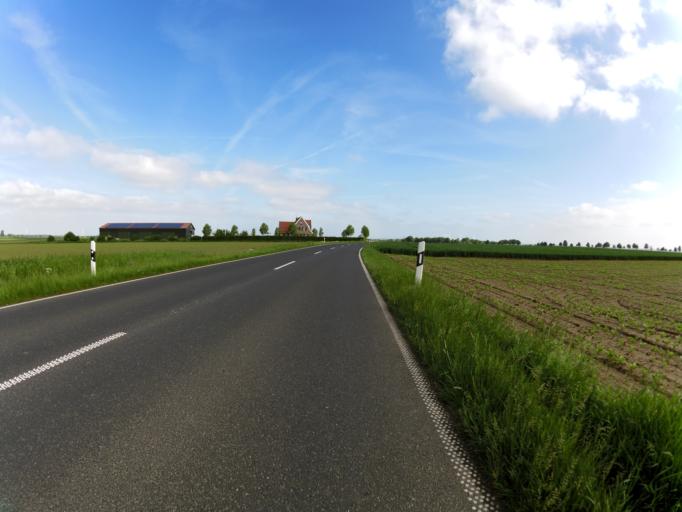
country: DE
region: North Rhine-Westphalia
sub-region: Regierungsbezirk Koln
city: Linnich
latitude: 50.9860
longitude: 6.2144
